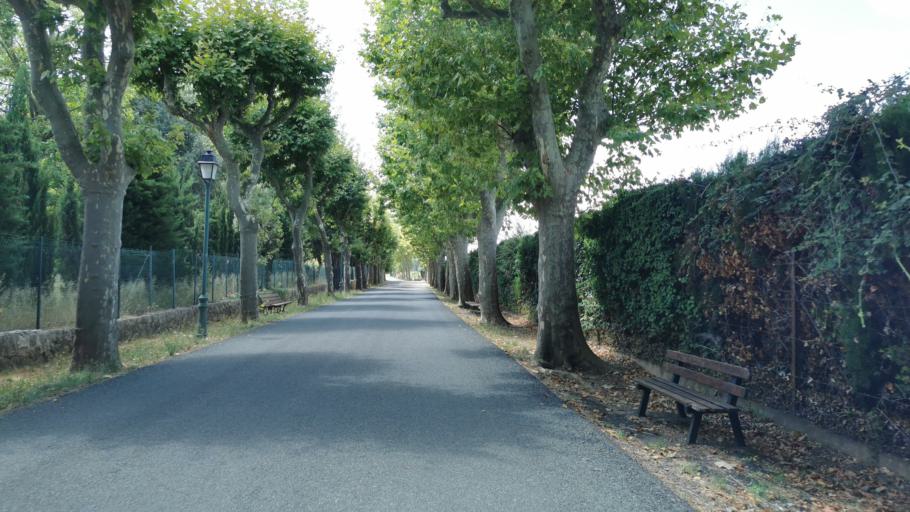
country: FR
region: Languedoc-Roussillon
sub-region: Departement de l'Aude
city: Bizanet
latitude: 43.1615
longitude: 2.8682
